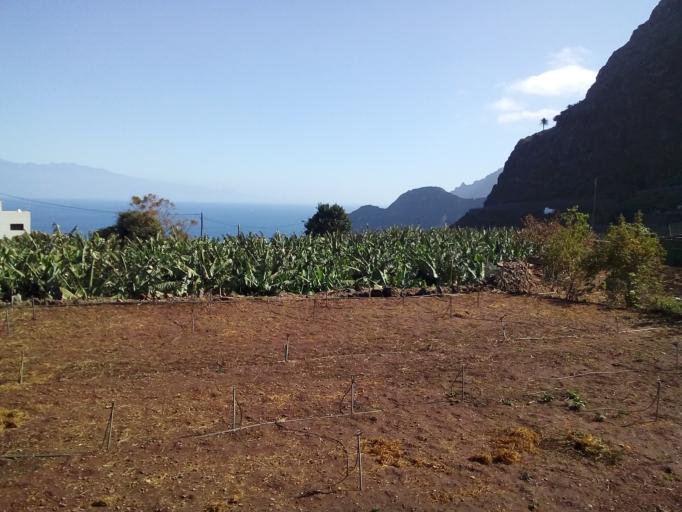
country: ES
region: Canary Islands
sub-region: Provincia de Santa Cruz de Tenerife
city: Agulo
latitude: 28.1880
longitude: -17.1938
